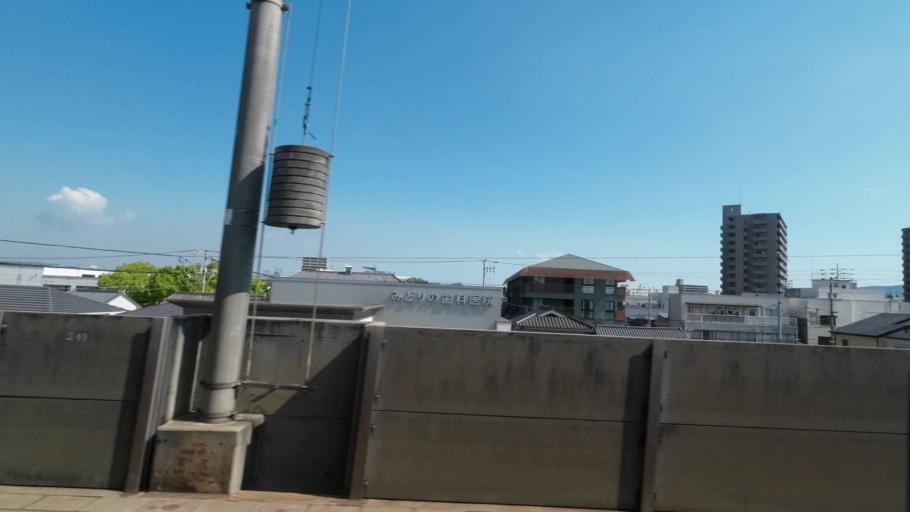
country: JP
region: Kagawa
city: Sakaidecho
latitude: 34.3130
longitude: 133.8501
